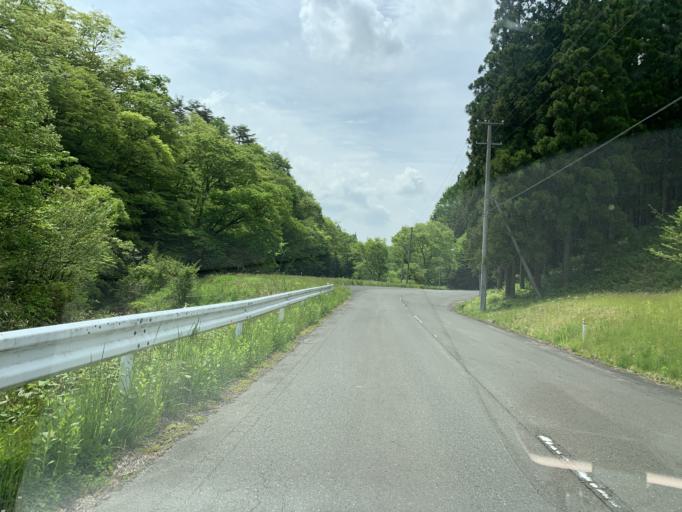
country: JP
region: Iwate
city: Ichinoseki
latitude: 38.8739
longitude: 140.9785
